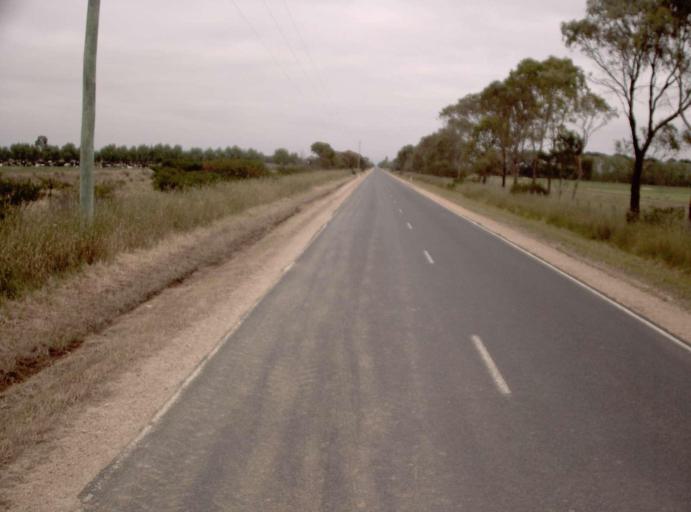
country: AU
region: Victoria
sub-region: Wellington
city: Heyfield
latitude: -38.0293
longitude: 146.9042
